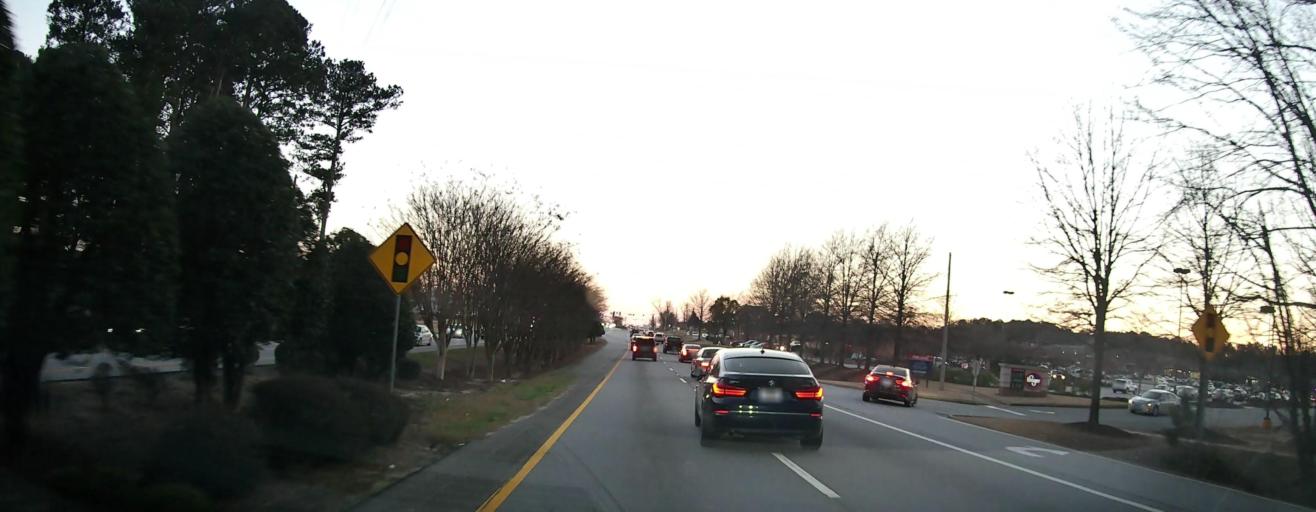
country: US
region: Georgia
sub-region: Fayette County
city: Fayetteville
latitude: 33.4706
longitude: -84.4454
